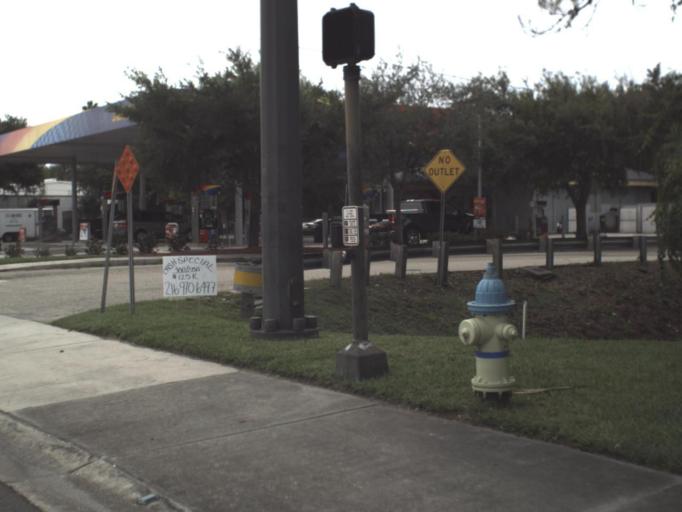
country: US
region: Florida
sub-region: Sarasota County
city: Sarasota Springs
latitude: 27.2989
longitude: -82.4891
